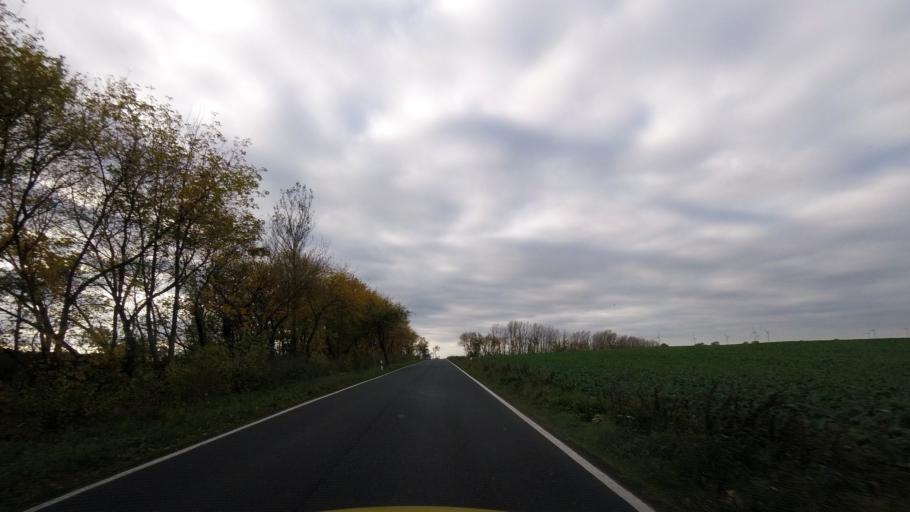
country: DE
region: Saxony-Anhalt
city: Zahna
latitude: 51.9731
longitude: 12.8409
